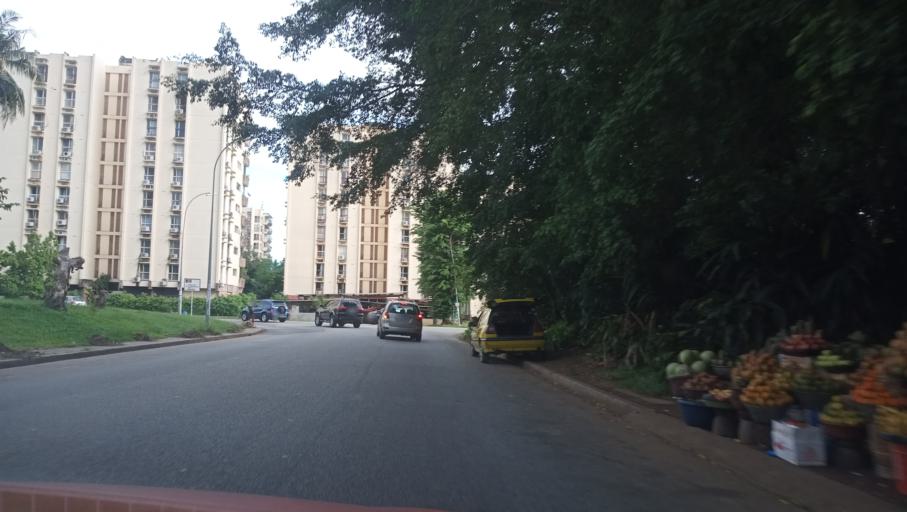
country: CI
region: Lagunes
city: Abidjan
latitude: 5.3415
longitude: -3.9788
